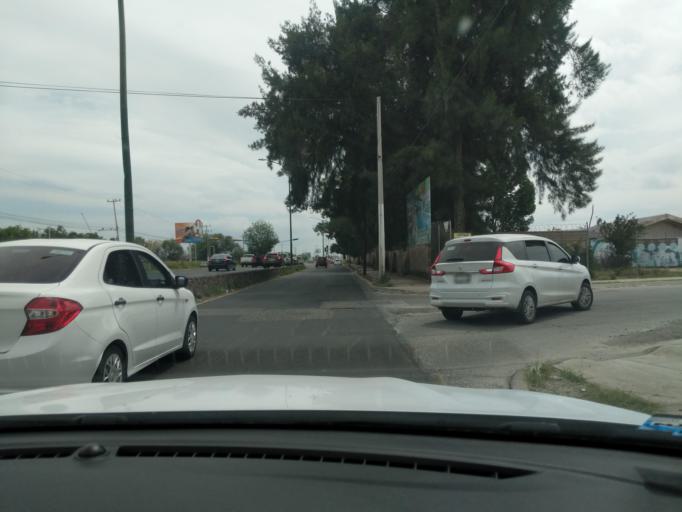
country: MX
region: Jalisco
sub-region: Zapopan
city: Puerta del Llano
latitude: 20.7850
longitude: -103.4681
